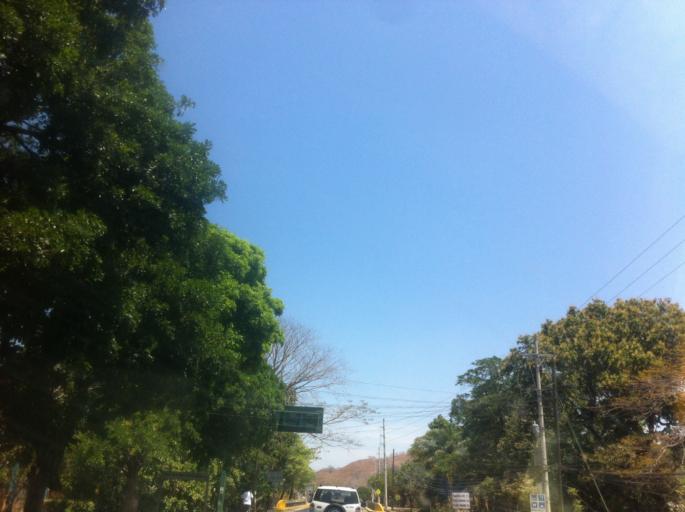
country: CR
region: Guanacaste
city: Belen
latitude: 10.3974
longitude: -85.5869
